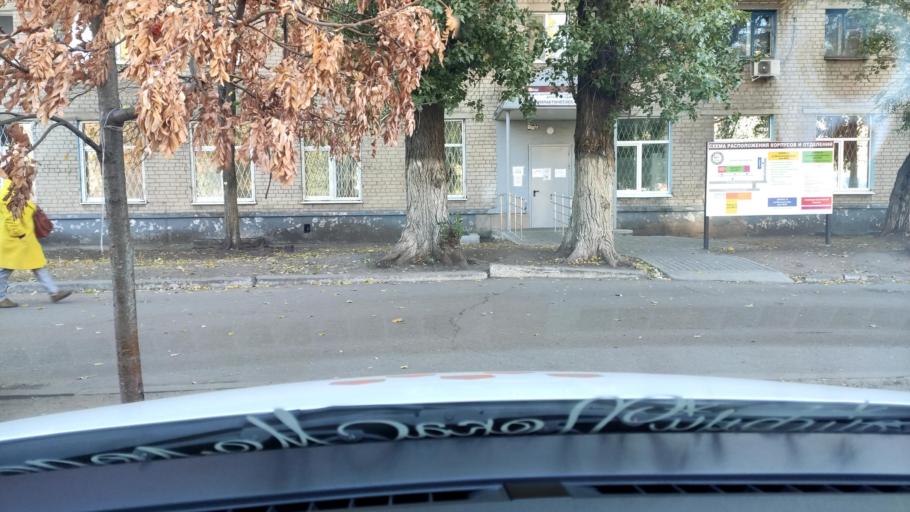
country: RU
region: Voronezj
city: Voronezh
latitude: 51.6746
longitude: 39.1564
